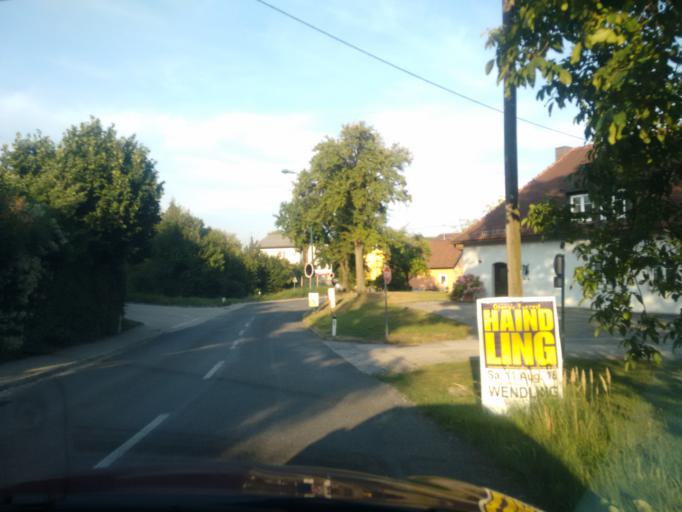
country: AT
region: Upper Austria
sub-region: Politischer Bezirk Vocklabruck
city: Niederthalheim
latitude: 48.1395
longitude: 13.7308
